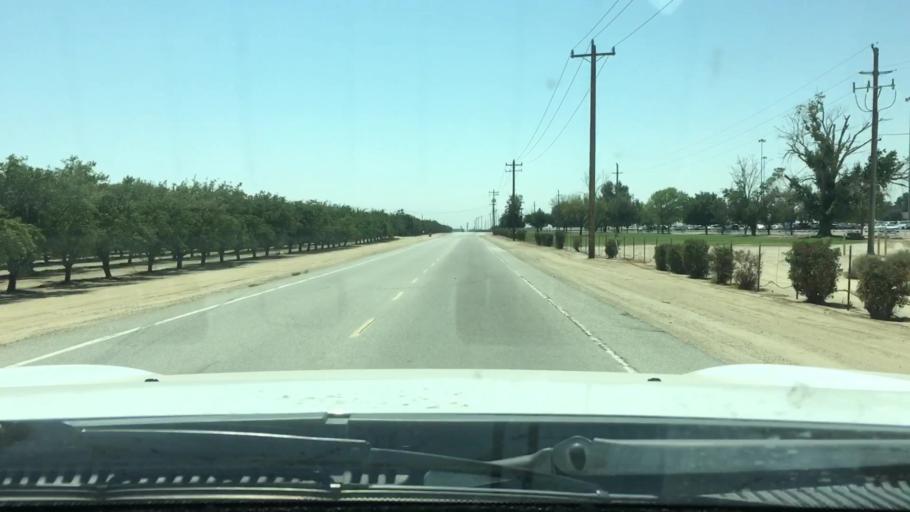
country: US
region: California
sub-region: Kern County
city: Wasco
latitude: 35.5964
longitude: -119.4026
